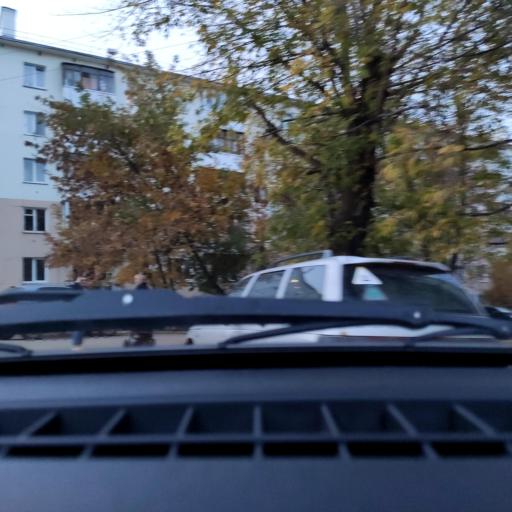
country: RU
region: Bashkortostan
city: Ufa
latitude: 54.7454
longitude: 55.9940
